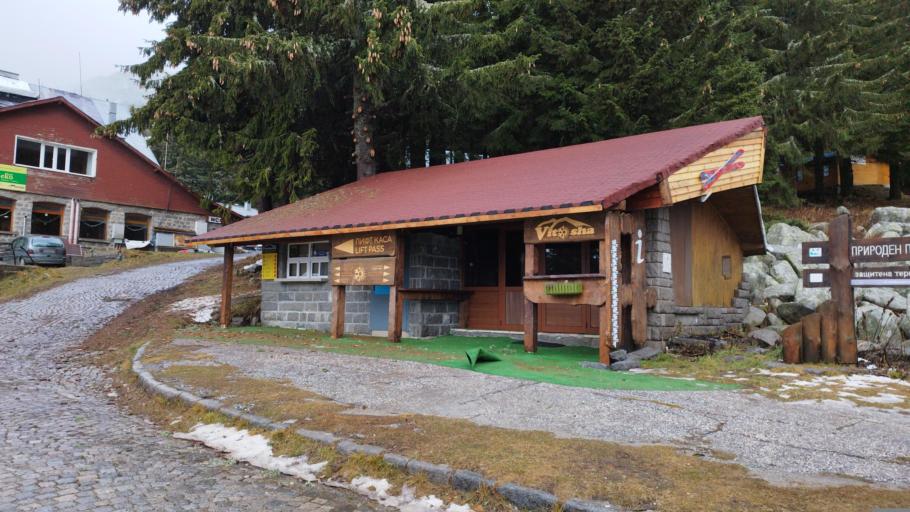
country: BG
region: Sofia-Capital
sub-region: Stolichna Obshtina
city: Sofia
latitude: 42.5831
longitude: 23.2921
